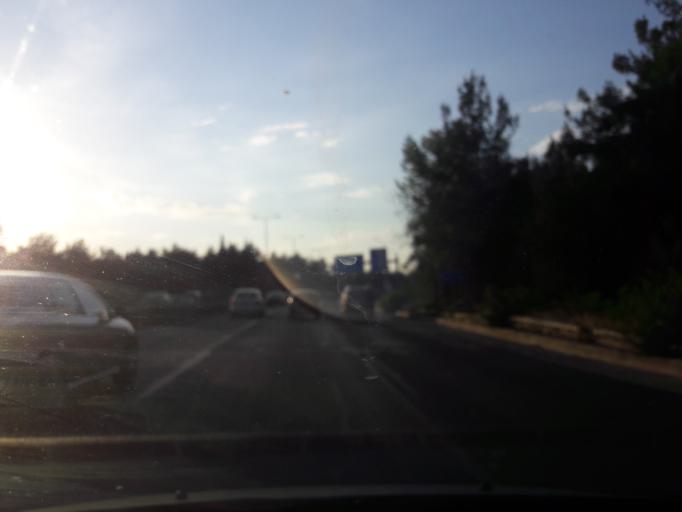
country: GR
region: Central Macedonia
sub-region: Nomos Thessalonikis
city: Triandria
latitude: 40.6161
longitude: 22.9851
